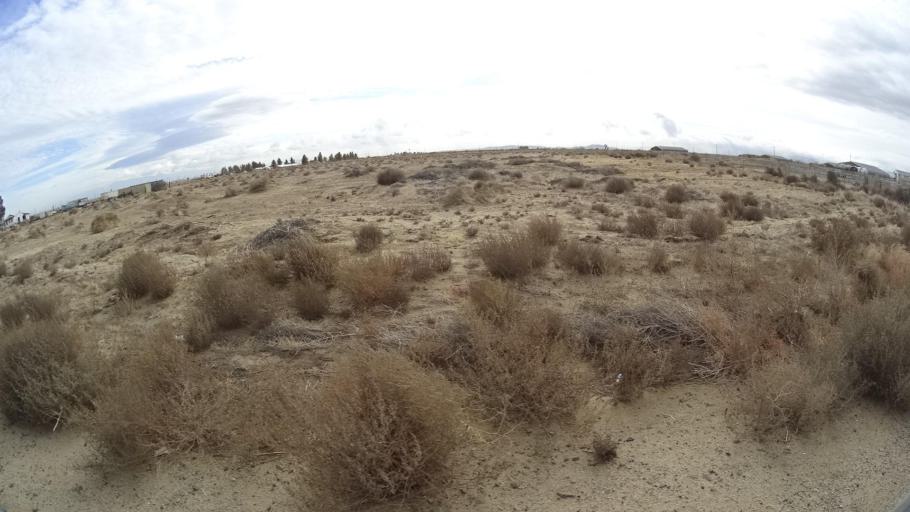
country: US
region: California
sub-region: Kern County
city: Rosamond
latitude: 34.8630
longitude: -118.3597
